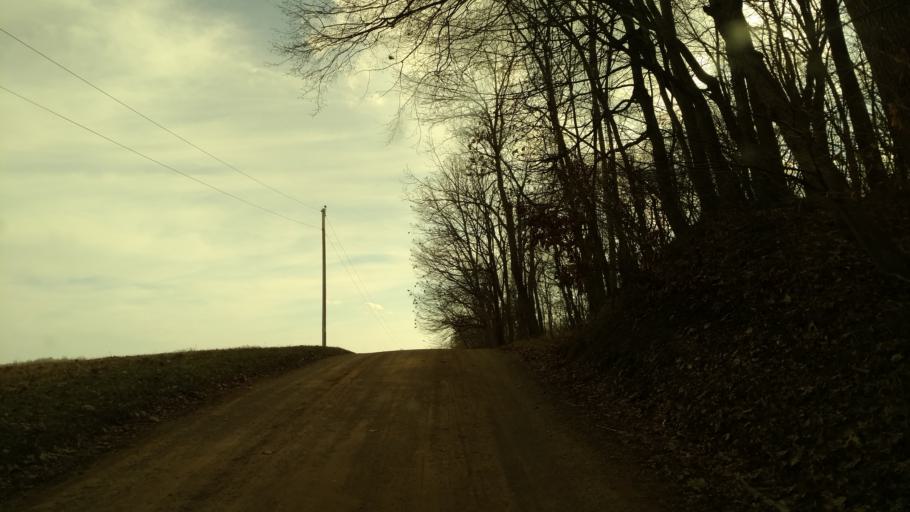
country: US
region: Ohio
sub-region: Ashland County
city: Loudonville
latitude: 40.5630
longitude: -82.3268
